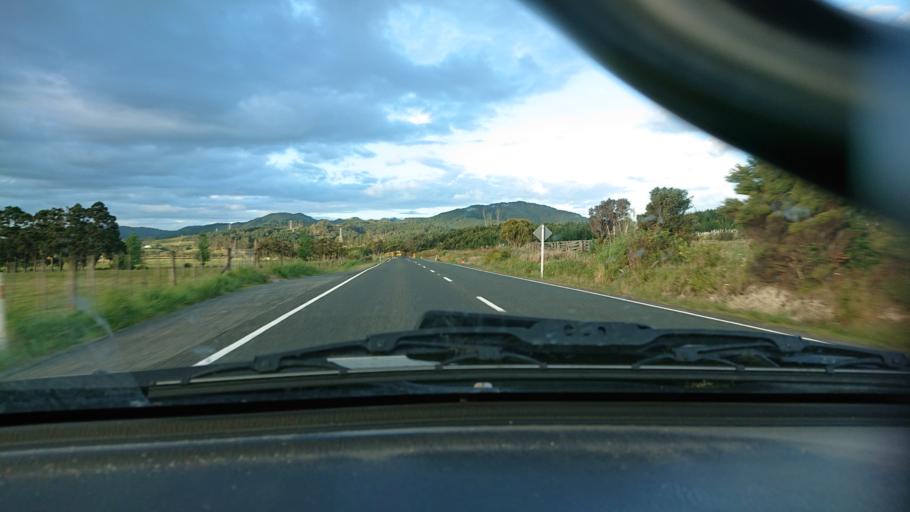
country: NZ
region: Auckland
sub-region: Auckland
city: Parakai
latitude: -36.5172
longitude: 174.4503
